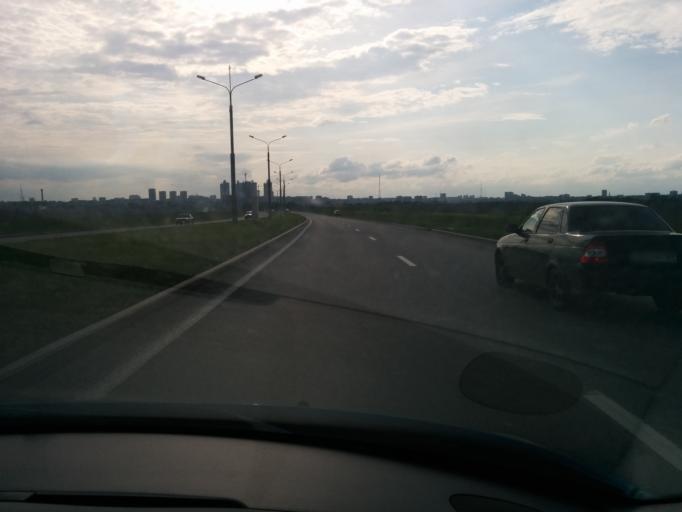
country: RU
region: Perm
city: Perm
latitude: 58.0064
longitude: 56.3568
